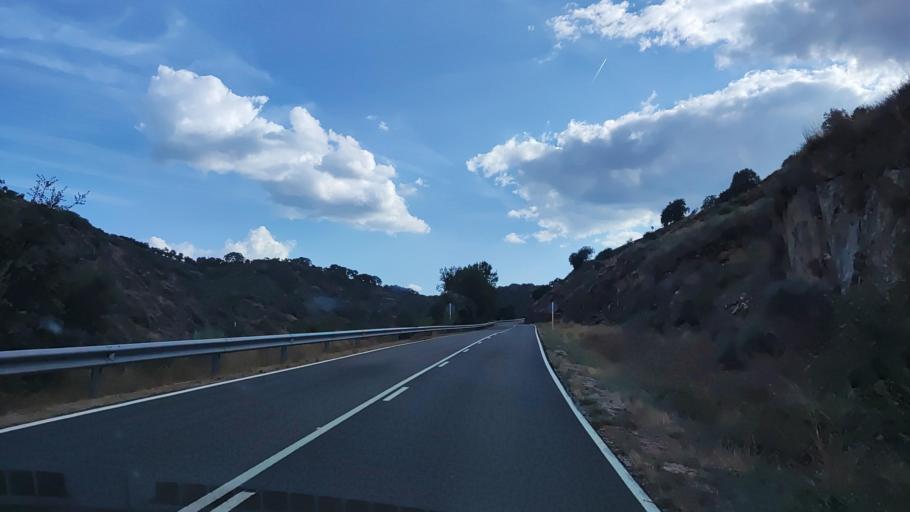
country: ES
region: Castille and Leon
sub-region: Provincia de Salamanca
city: Pastores
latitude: 40.4960
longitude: -6.4973
